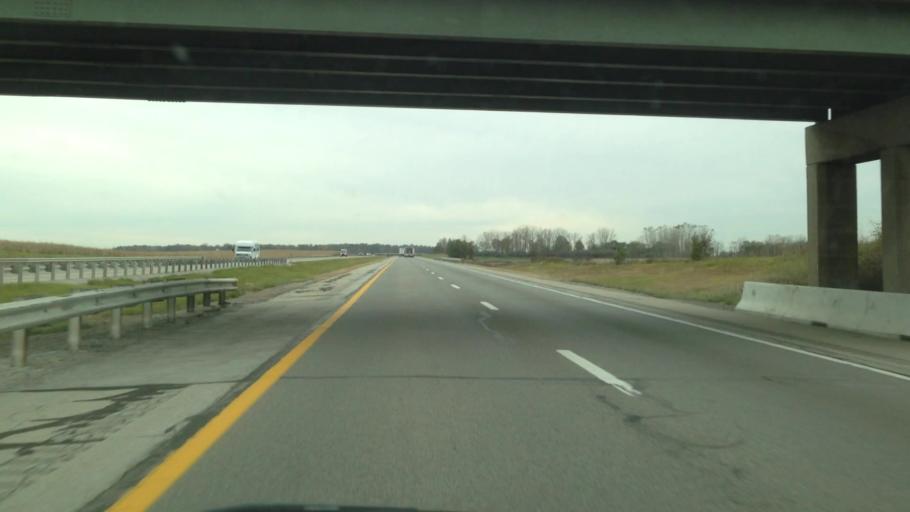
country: US
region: Ohio
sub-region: Williams County
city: Montpelier
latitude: 41.6175
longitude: -84.6596
